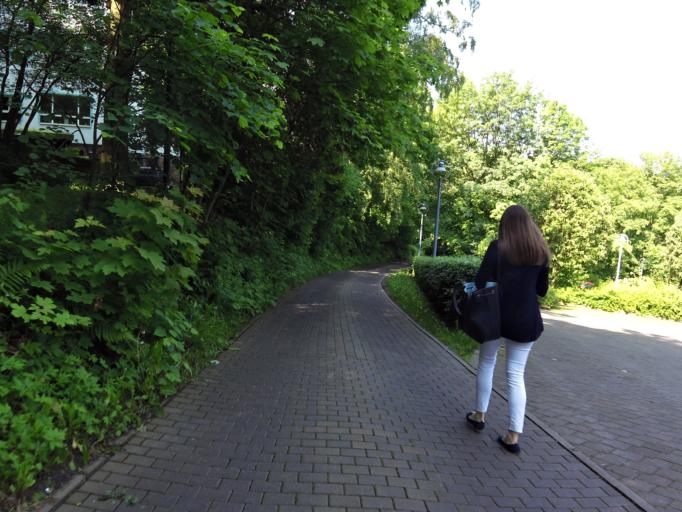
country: DE
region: Thuringia
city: Friedrichroda
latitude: 50.8614
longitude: 10.5635
